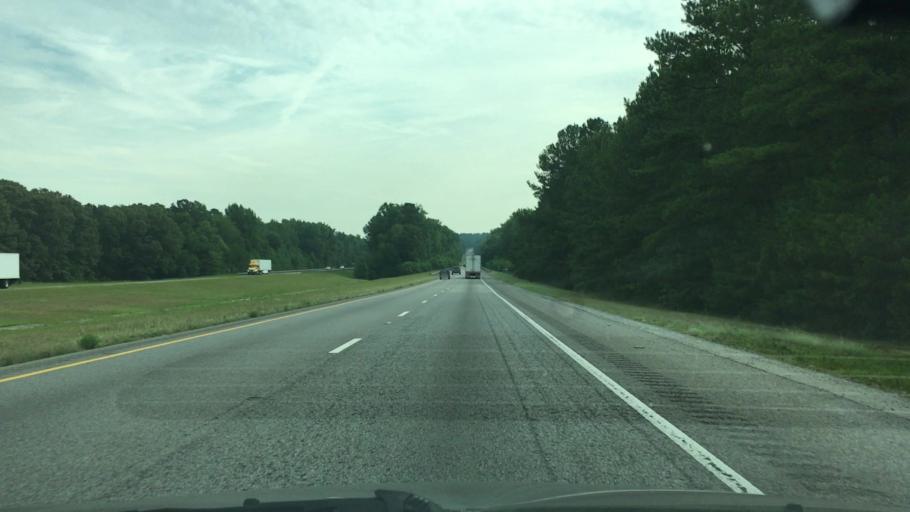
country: US
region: South Carolina
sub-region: Aiken County
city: Aiken
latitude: 33.6898
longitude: -81.6153
